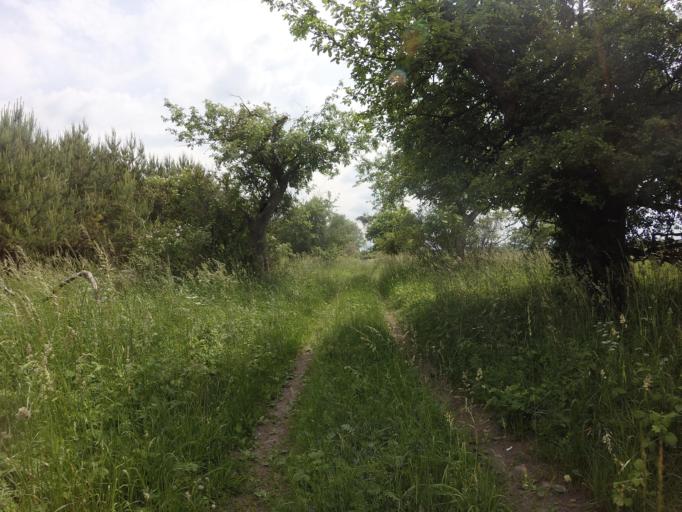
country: PL
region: West Pomeranian Voivodeship
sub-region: Powiat stargardzki
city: Dobrzany
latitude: 53.3387
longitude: 15.4446
